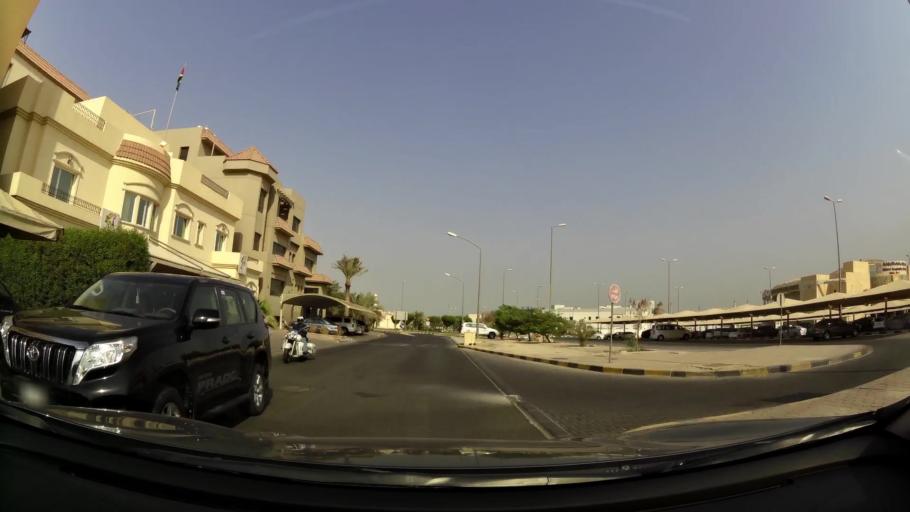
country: KW
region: Mubarak al Kabir
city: Sabah as Salim
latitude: 29.2740
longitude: 48.0440
